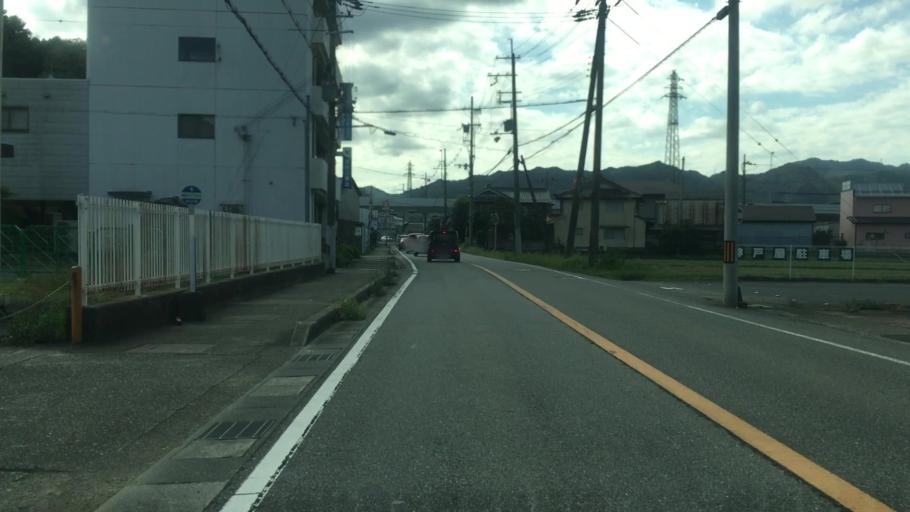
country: JP
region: Kyoto
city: Fukuchiyama
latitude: 35.1537
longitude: 135.0526
